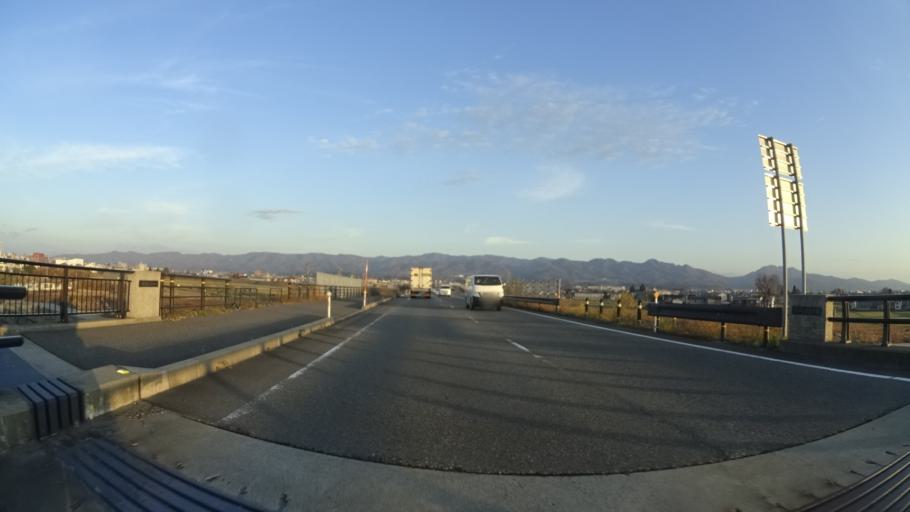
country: JP
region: Niigata
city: Nagaoka
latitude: 37.4297
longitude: 138.8262
